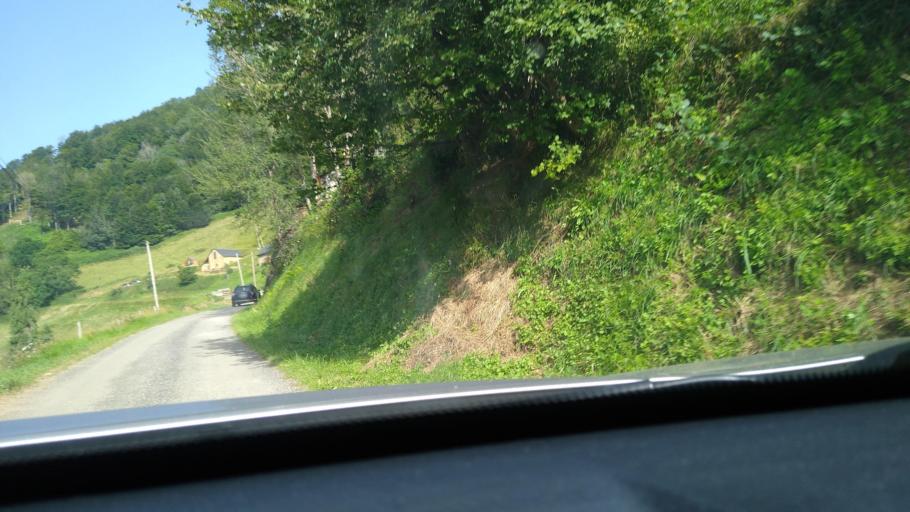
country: FR
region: Midi-Pyrenees
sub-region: Departement de l'Ariege
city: Saint-Girons
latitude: 42.7930
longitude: 1.1692
